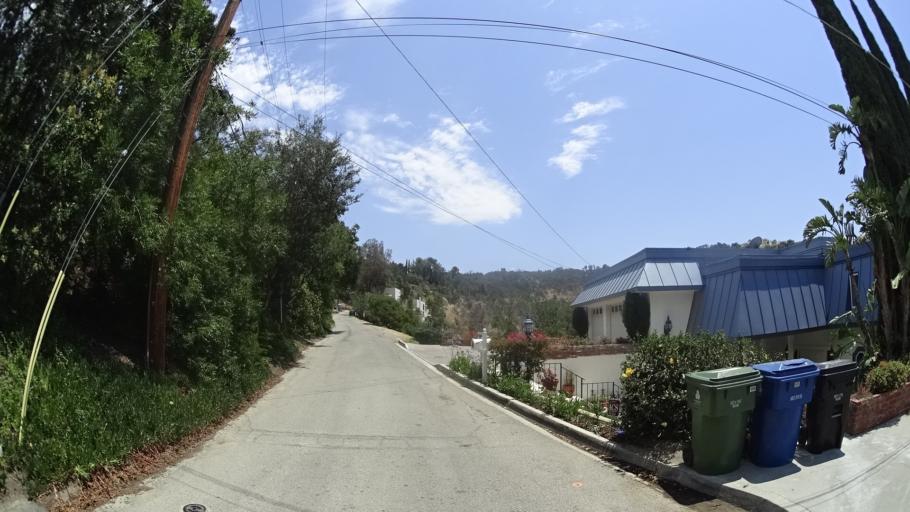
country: US
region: California
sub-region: Los Angeles County
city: Sherman Oaks
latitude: 34.1399
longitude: -118.4266
